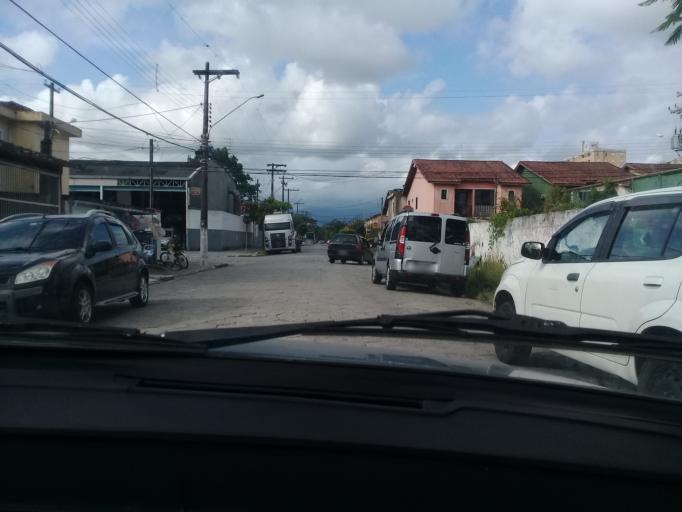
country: BR
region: Sao Paulo
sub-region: Guaruja
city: Guaruja
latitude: -23.9904
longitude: -46.2817
